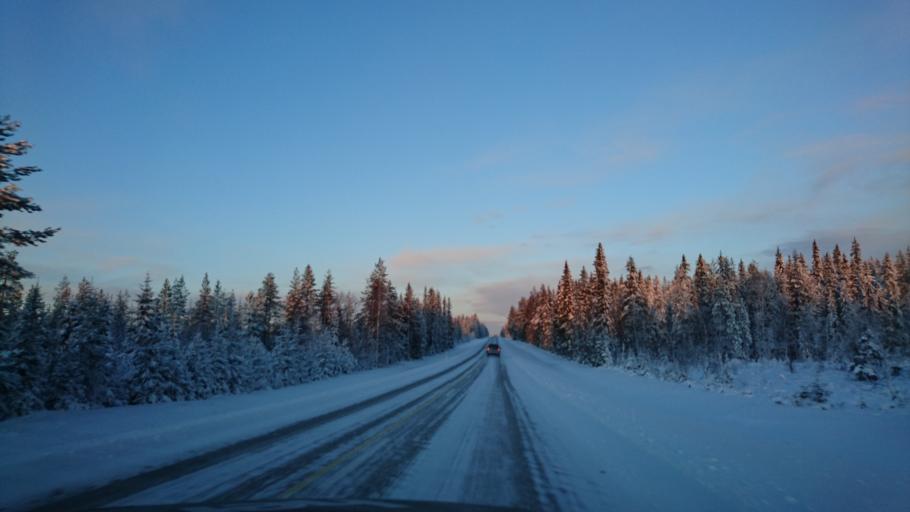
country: FI
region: Lapland
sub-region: Rovaniemi
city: Ranua
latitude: 65.7900
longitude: 26.5694
